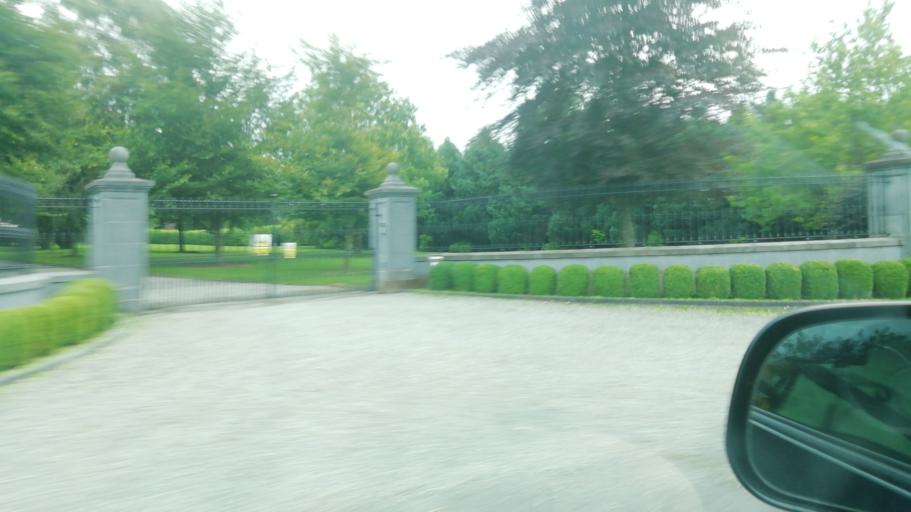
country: IE
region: Munster
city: Fethard
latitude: 52.4785
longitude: -7.6926
